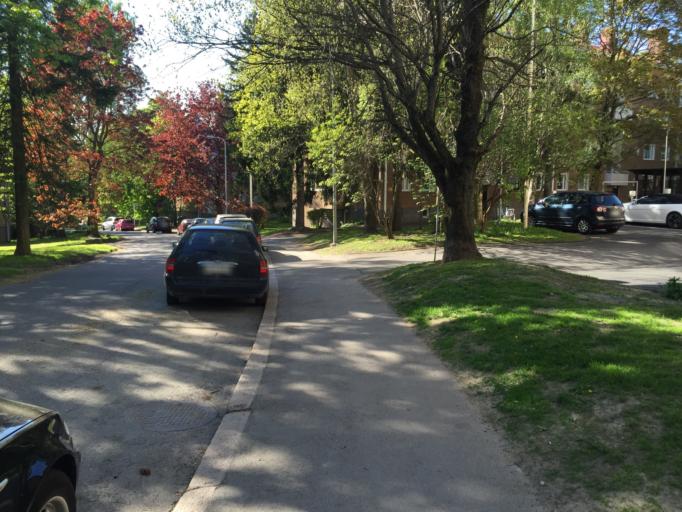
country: FI
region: Uusimaa
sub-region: Helsinki
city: Teekkarikylae
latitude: 60.1612
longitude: 24.8632
